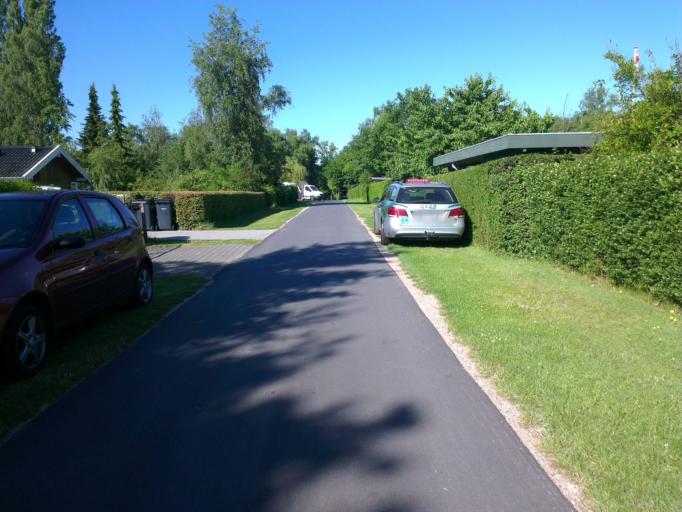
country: DK
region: Capital Region
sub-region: Frederikssund Kommune
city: Jaegerspris
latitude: 55.9145
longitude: 11.9211
